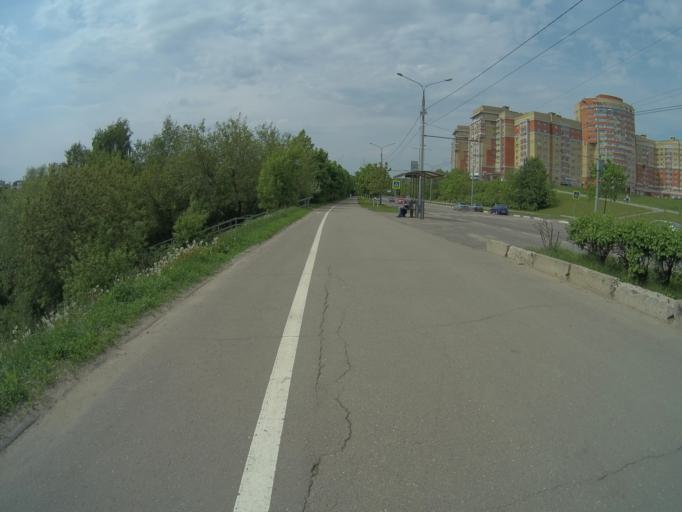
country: RU
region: Vladimir
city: Vladimir
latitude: 56.1361
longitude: 40.3855
